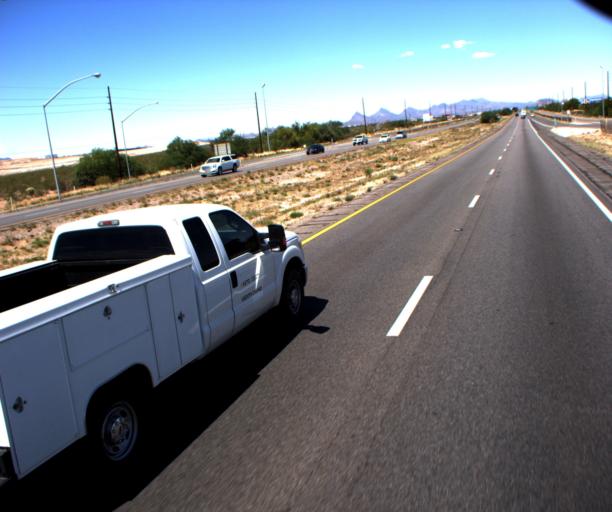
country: US
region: Arizona
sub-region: Pima County
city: Summit
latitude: 32.1170
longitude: -110.8617
